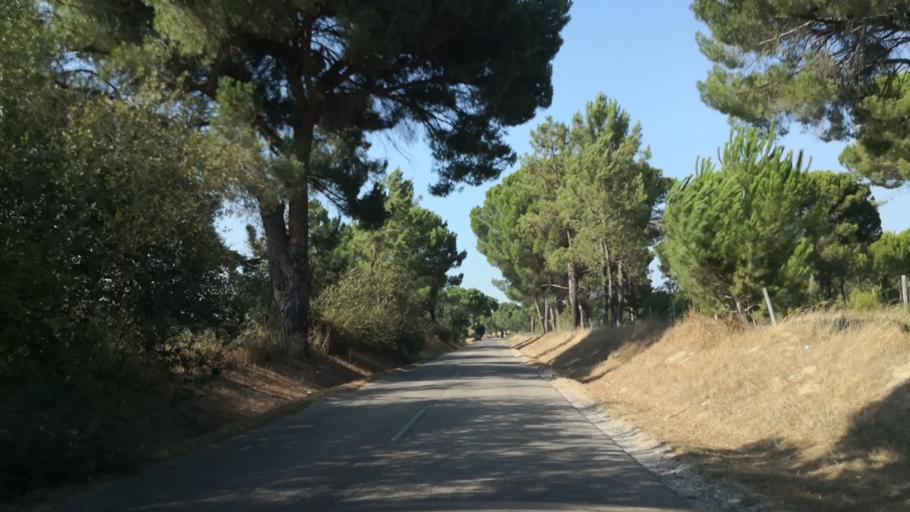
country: PT
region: Santarem
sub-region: Coruche
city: Coruche
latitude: 38.8905
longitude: -8.5343
